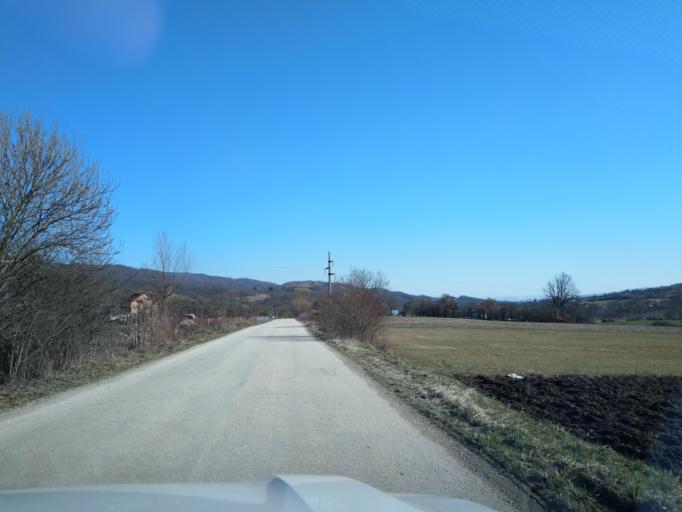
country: RS
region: Central Serbia
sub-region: Zlatiborski Okrug
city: Kosjeric
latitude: 43.9306
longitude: 19.8942
